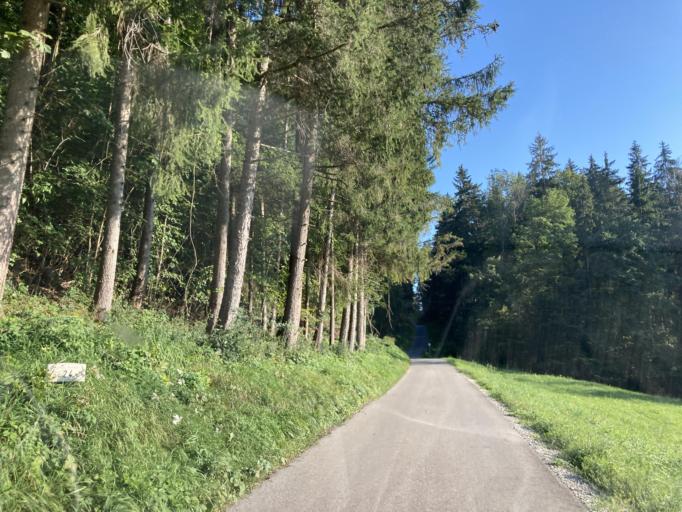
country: DE
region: Baden-Wuerttemberg
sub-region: Freiburg Region
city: Blumberg
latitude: 47.8235
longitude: 8.5106
